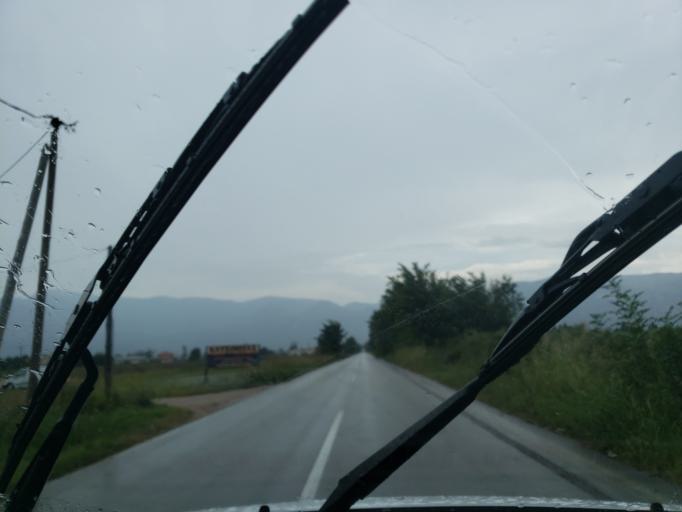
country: GR
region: Central Greece
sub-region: Nomos Fthiotidos
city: Anthili
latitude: 38.8380
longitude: 22.4411
